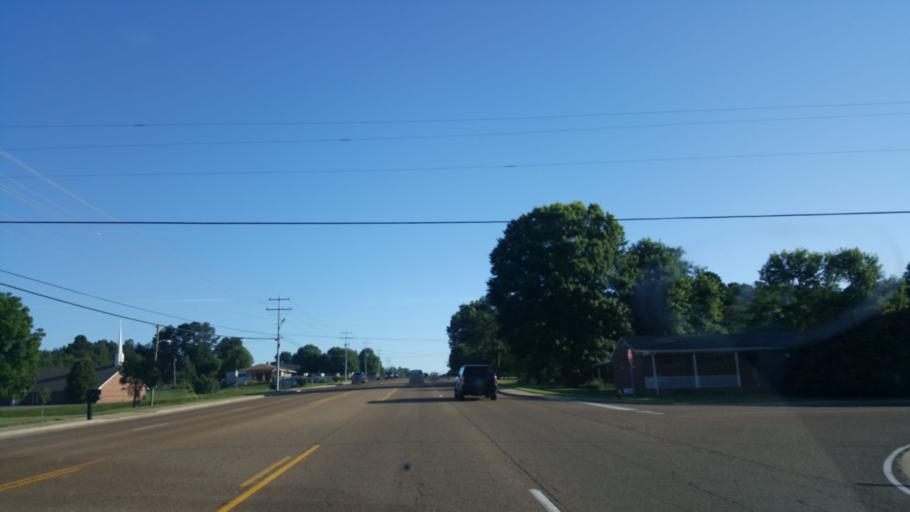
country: US
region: Tennessee
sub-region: Henderson County
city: Lexington
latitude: 35.6772
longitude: -88.3852
